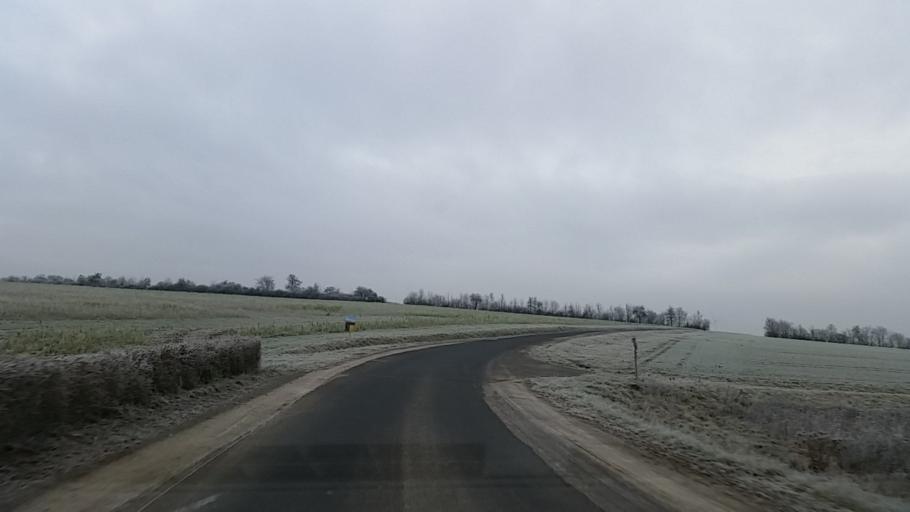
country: DE
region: Bavaria
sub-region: Regierungsbezirk Unterfranken
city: Fuchsstadt
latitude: 50.0389
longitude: 9.9069
